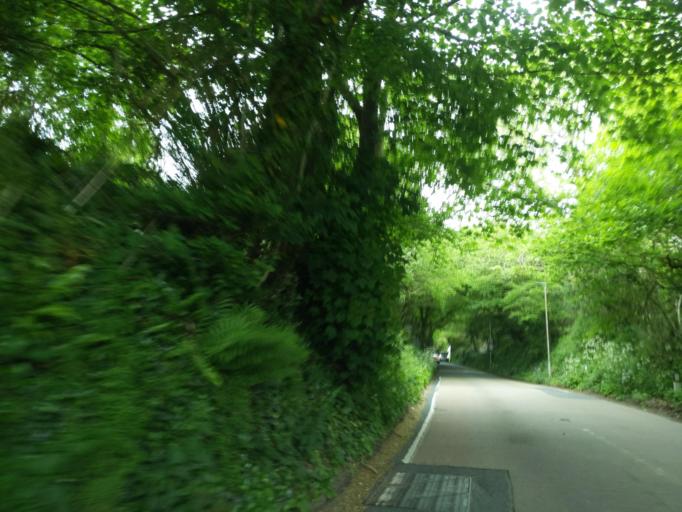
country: GB
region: England
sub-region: Devon
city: Plympton
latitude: 50.3996
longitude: -4.0537
